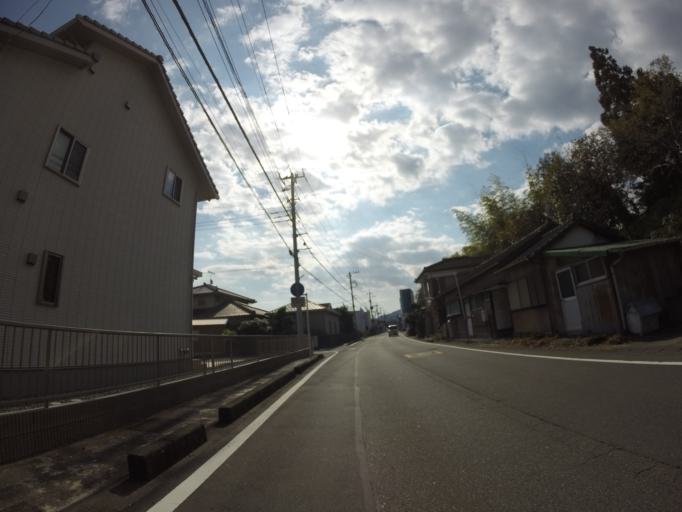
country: JP
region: Shizuoka
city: Fujinomiya
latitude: 35.1764
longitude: 138.6364
